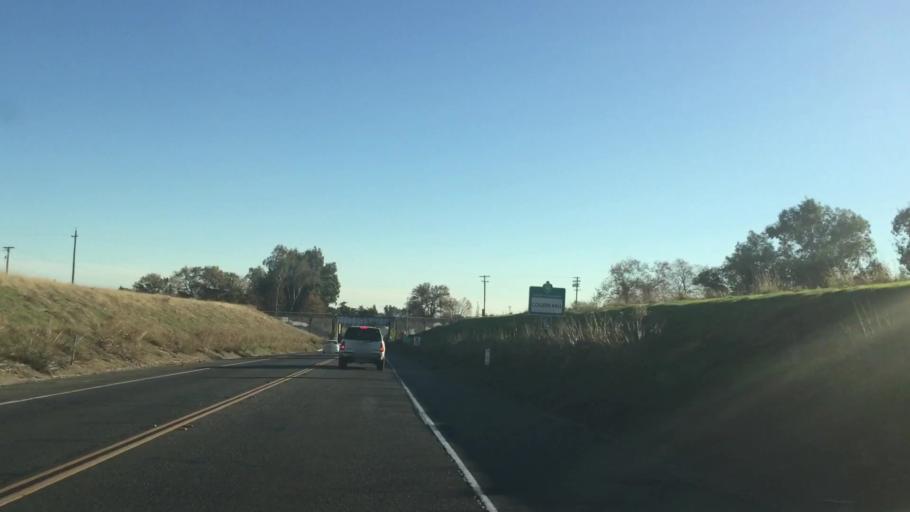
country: US
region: California
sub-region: Yuba County
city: Marysville
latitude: 39.1605
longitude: -121.5904
